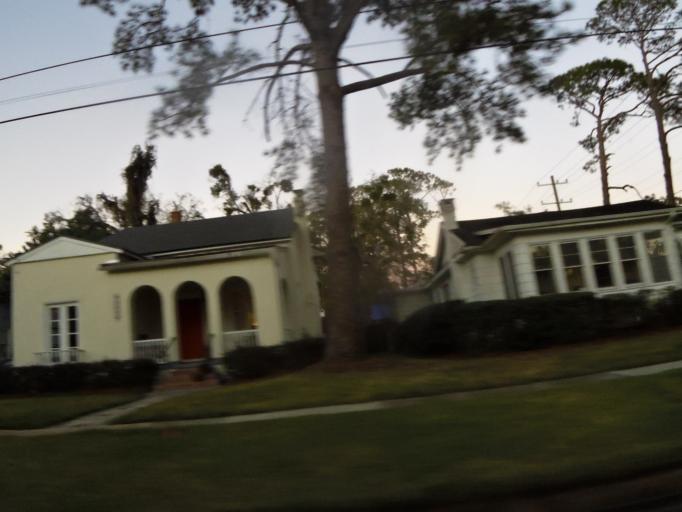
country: US
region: Florida
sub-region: Duval County
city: Jacksonville
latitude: 30.3077
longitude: -81.7114
